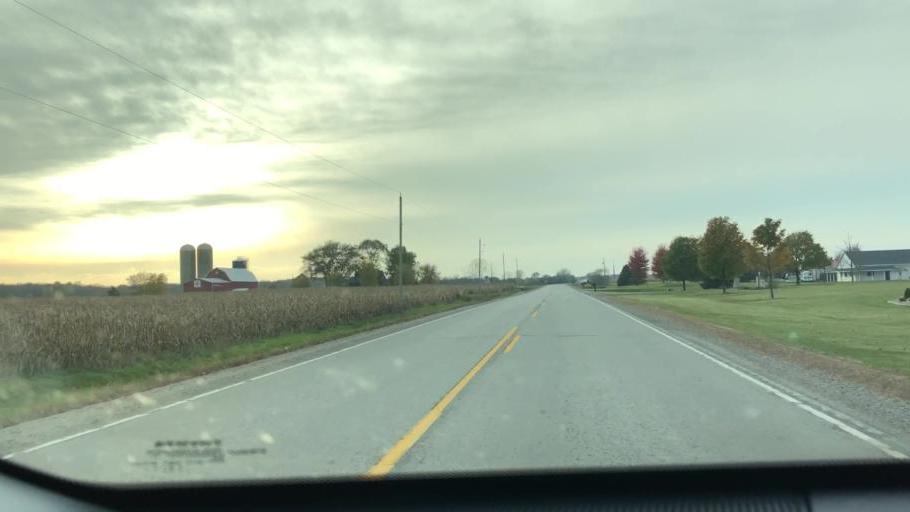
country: US
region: Wisconsin
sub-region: Outagamie County
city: Seymour
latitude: 44.4436
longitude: -88.3333
